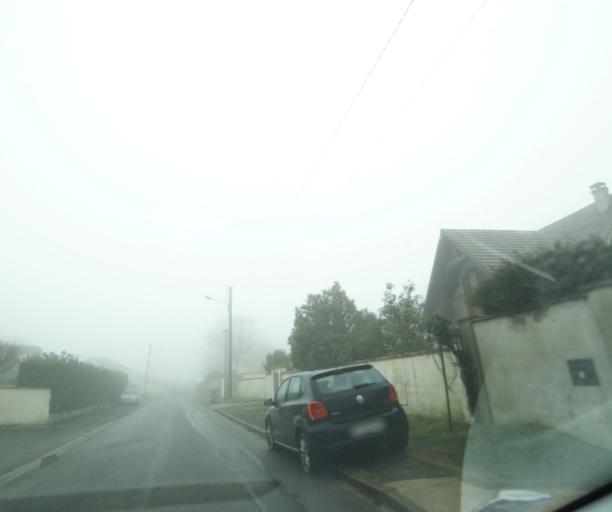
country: FR
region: Ile-de-France
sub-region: Departement de Seine-et-Marne
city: Dammartin-en-Goele
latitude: 49.0524
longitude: 2.6893
